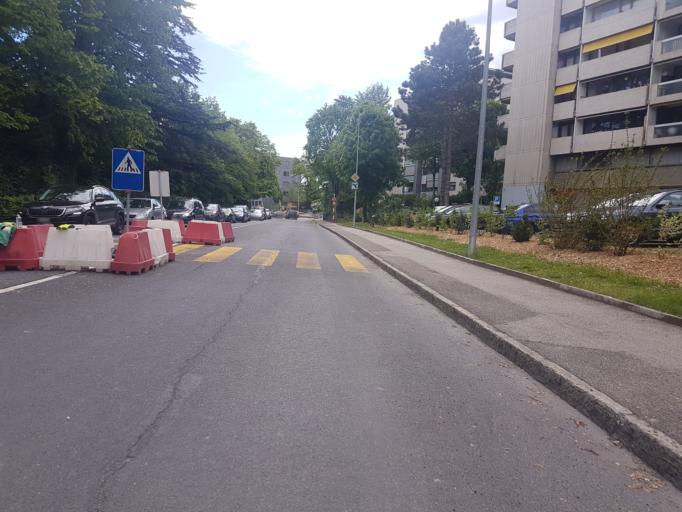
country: CH
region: Geneva
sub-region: Geneva
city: Versoix
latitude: 46.2834
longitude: 6.1658
